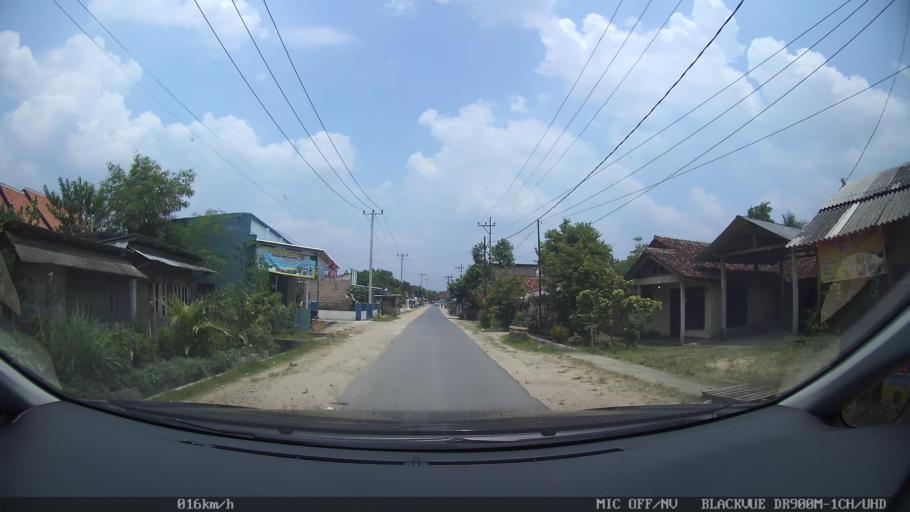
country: ID
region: Lampung
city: Pringsewu
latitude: -5.3487
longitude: 104.9858
